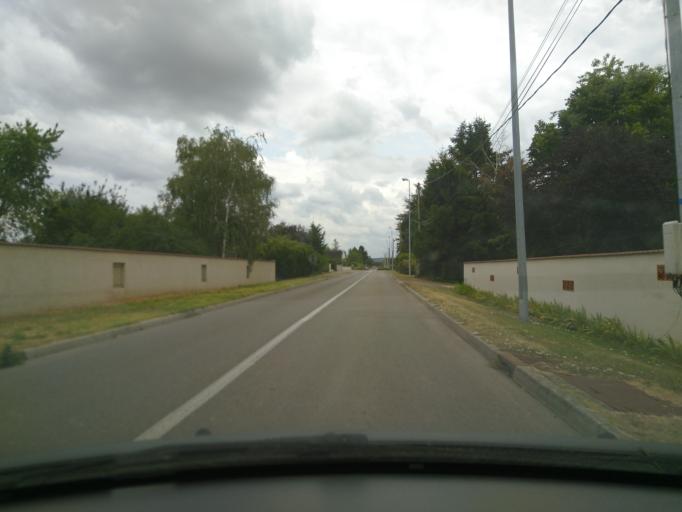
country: FR
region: Rhone-Alpes
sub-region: Departement de l'Isere
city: Beaurepaire
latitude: 45.3528
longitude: 5.0352
